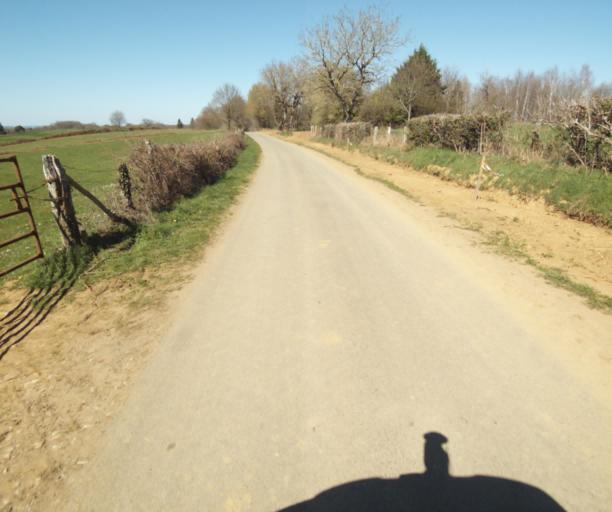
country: FR
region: Limousin
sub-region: Departement de la Correze
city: Saint-Clement
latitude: 45.3767
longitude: 1.6787
